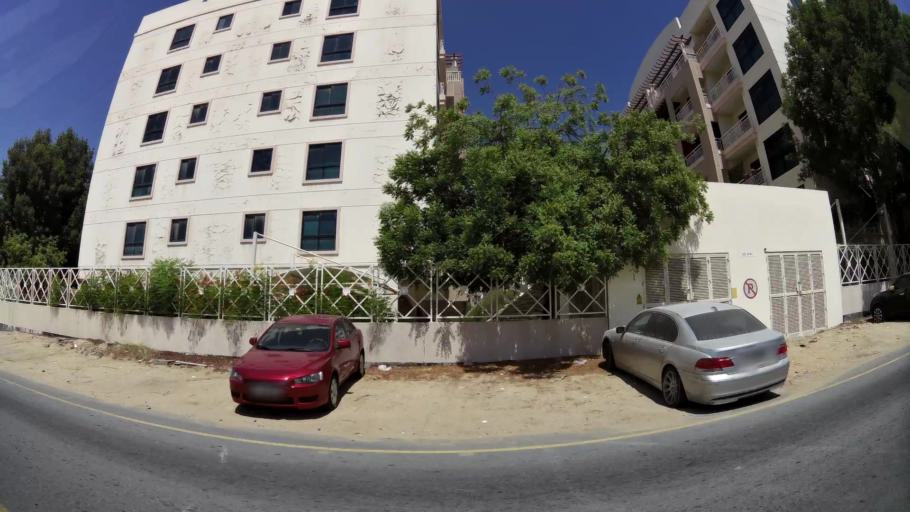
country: AE
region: Dubai
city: Dubai
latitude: 24.9855
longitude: 55.2038
